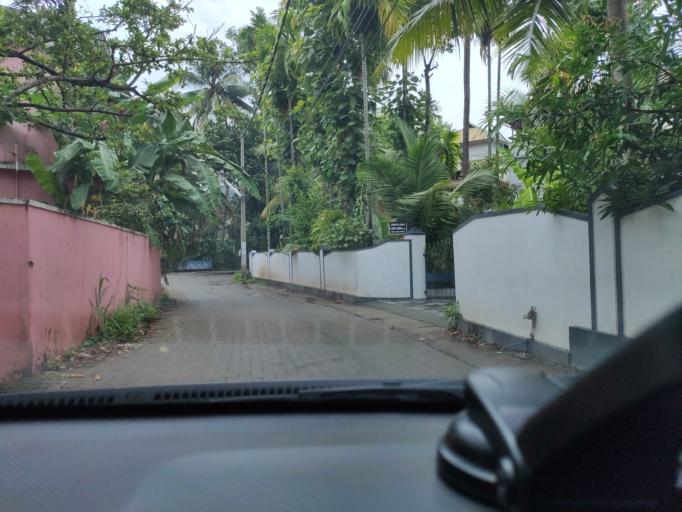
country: IN
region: Kerala
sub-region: Ernakulam
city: Elur
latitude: 10.0275
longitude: 76.3305
